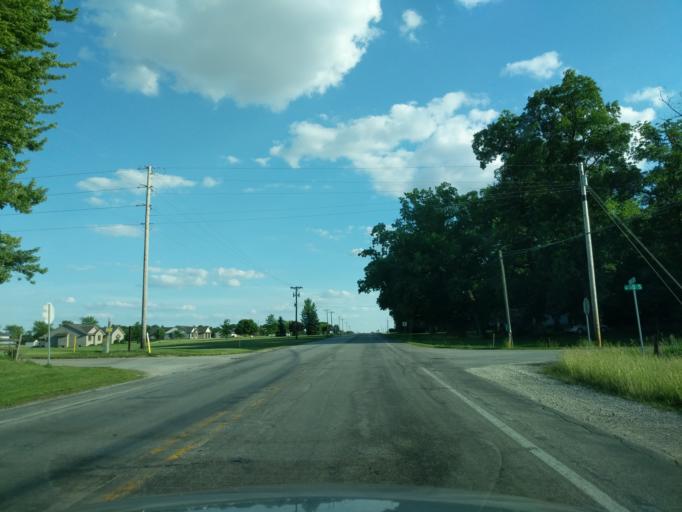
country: US
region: Indiana
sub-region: Whitley County
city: Columbia City
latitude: 41.1040
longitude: -85.4715
